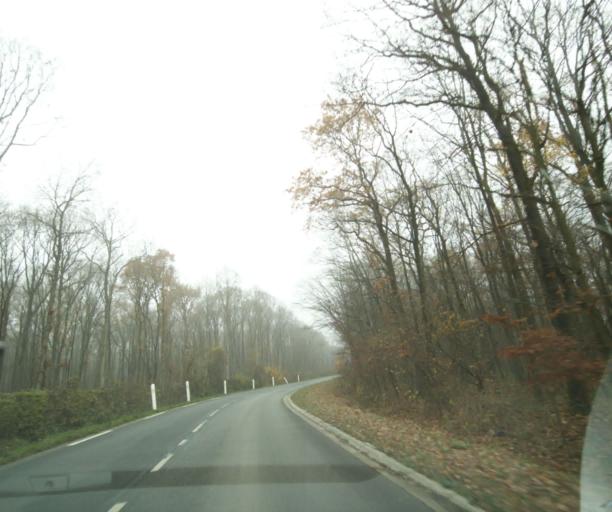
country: FR
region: Ile-de-France
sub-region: Departement de Seine-Saint-Denis
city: Vaujours
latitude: 48.9226
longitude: 2.5607
